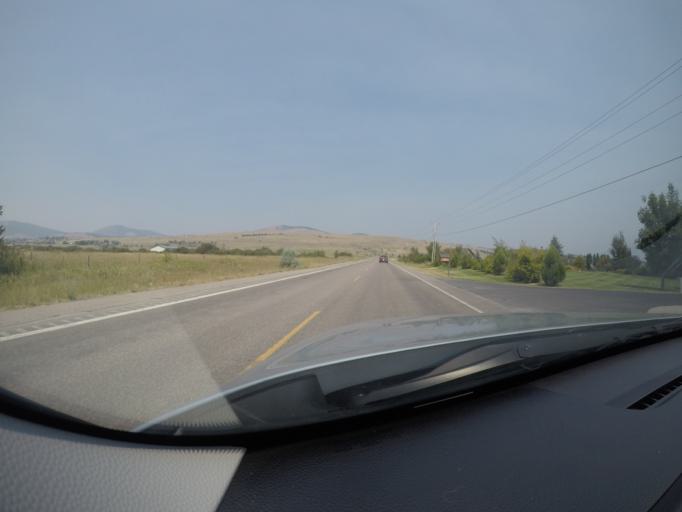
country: US
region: Montana
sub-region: Lake County
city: Polson
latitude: 47.7271
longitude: -114.1887
